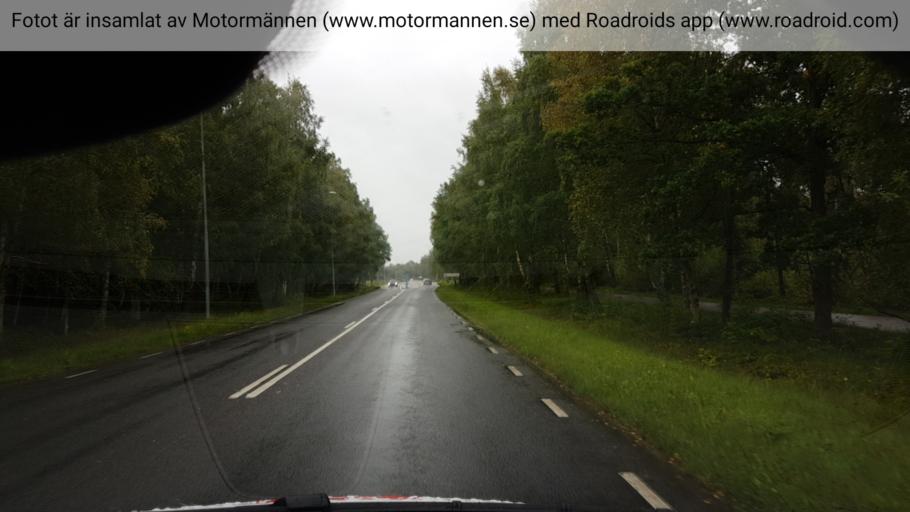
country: SE
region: Halland
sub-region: Halmstads Kommun
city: Mjallby
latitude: 56.6554
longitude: 12.7706
